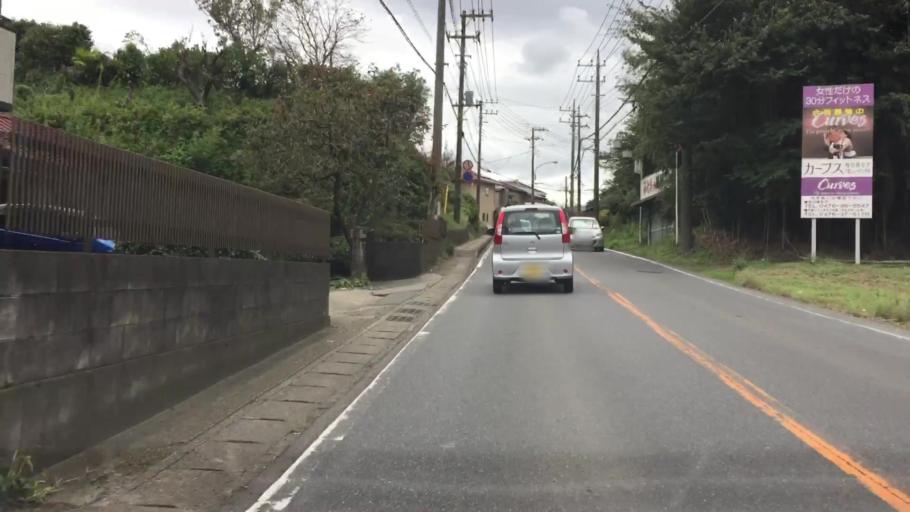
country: JP
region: Ibaraki
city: Ryugasaki
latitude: 35.8321
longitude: 140.1429
